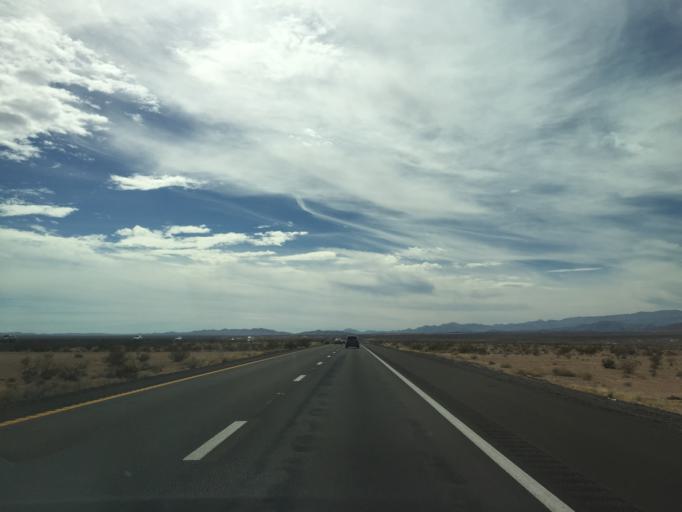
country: US
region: Nevada
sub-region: Clark County
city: Moapa Town
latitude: 36.5734
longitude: -114.6669
